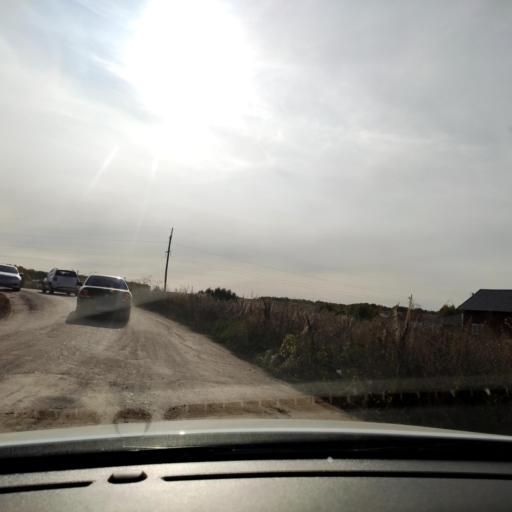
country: RU
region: Tatarstan
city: Vysokaya Gora
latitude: 55.8643
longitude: 49.3664
